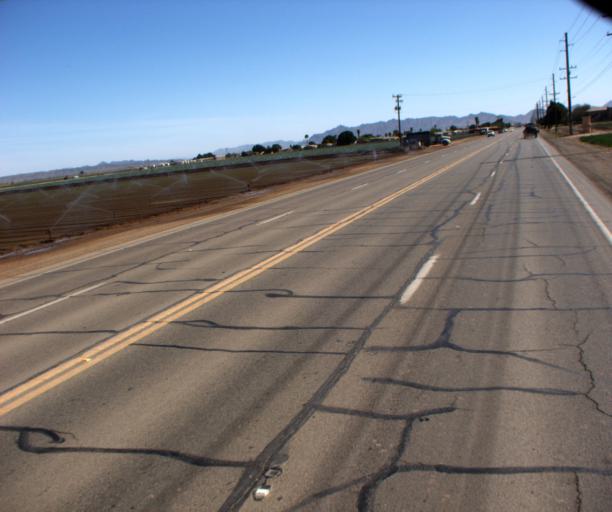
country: US
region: Arizona
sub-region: Yuma County
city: Yuma
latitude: 32.6991
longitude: -114.5358
